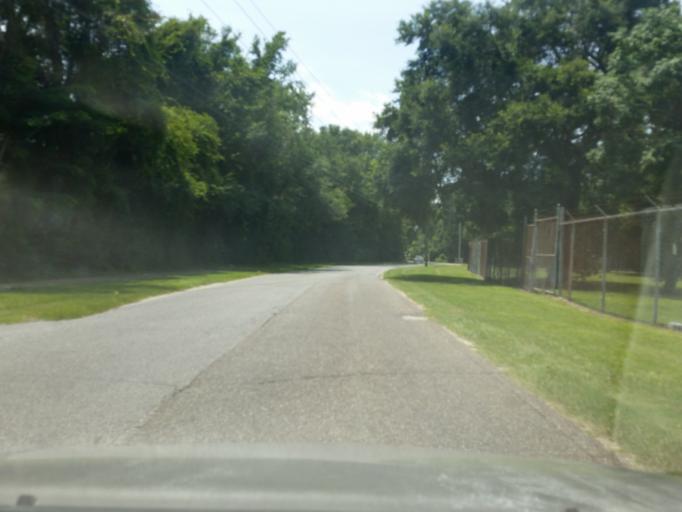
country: US
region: Florida
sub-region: Escambia County
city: Ferry Pass
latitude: 30.4994
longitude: -87.2173
